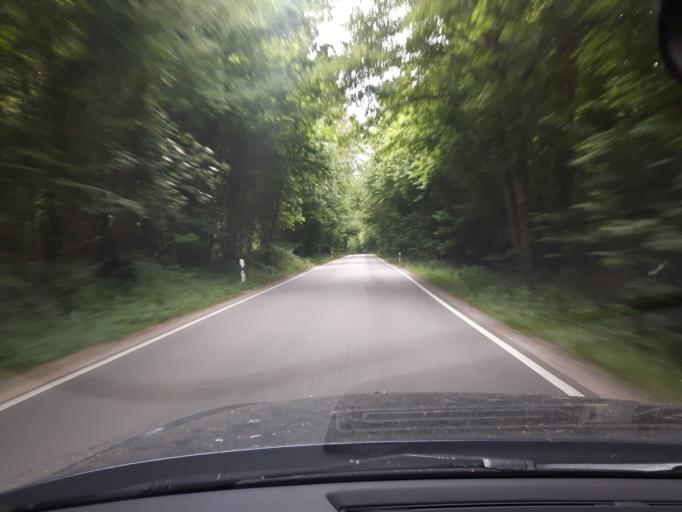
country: DE
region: Schleswig-Holstein
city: Ratekau
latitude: 53.9256
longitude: 10.7872
